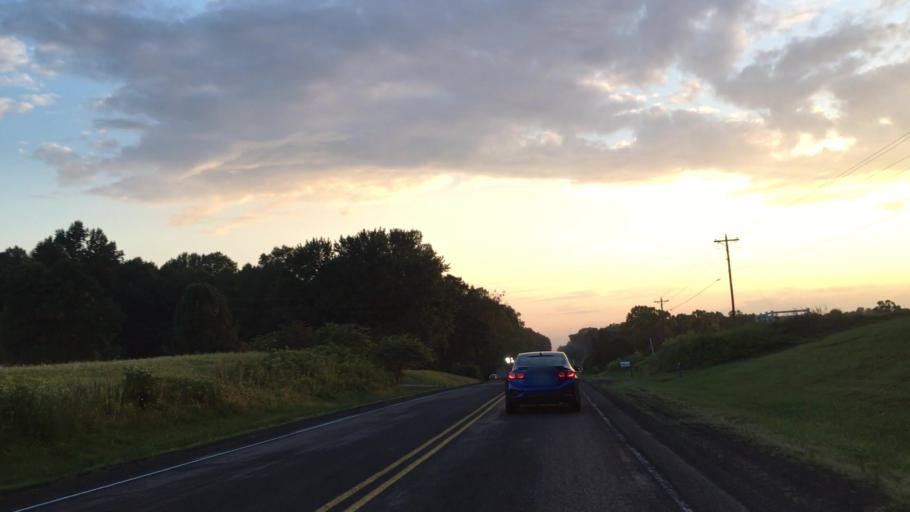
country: US
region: Virginia
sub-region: Spotsylvania County
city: Spotsylvania
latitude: 38.3096
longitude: -77.7898
